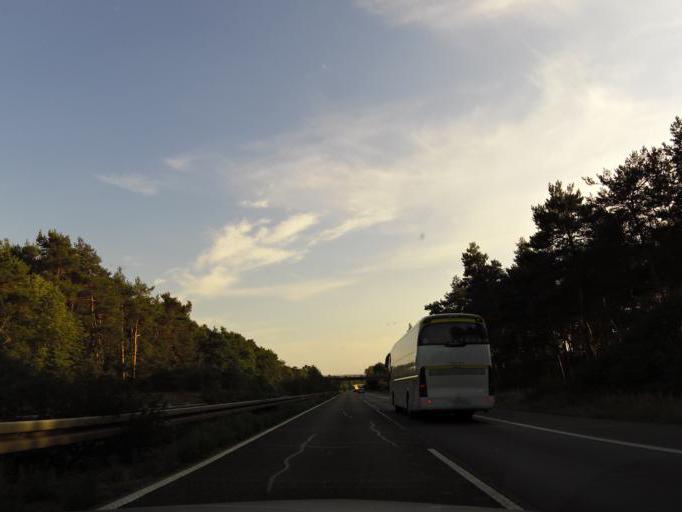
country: DE
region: Hesse
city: Griesheim
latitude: 49.8413
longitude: 8.5945
